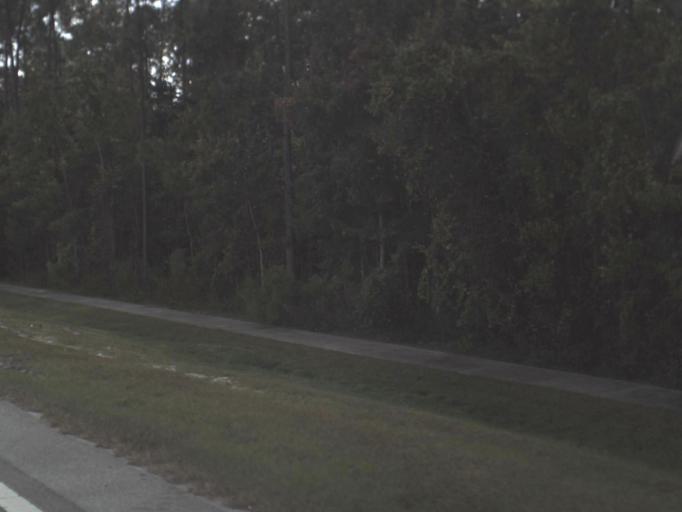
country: US
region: Florida
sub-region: Osceola County
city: Celebration
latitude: 28.3145
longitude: -81.4855
